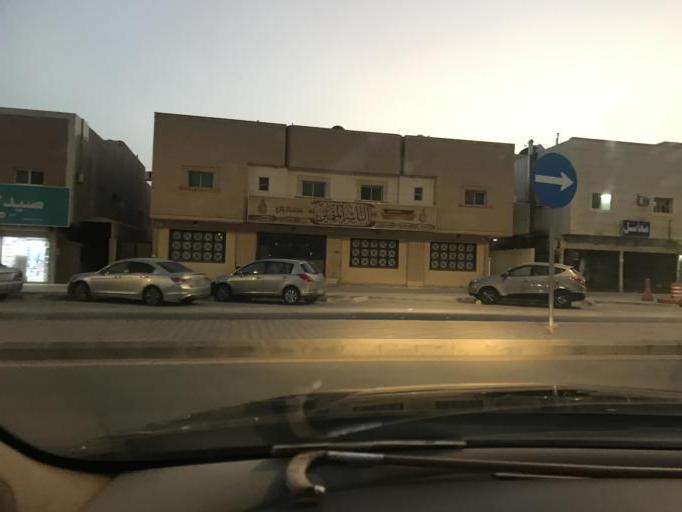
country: SA
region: Ar Riyad
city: Riyadh
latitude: 24.8034
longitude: 46.7065
